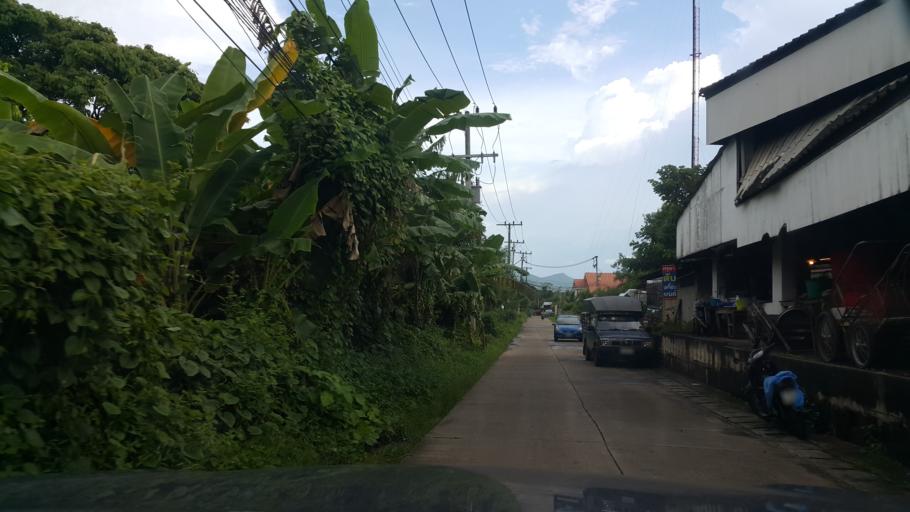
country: TH
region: Lampang
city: Thoen
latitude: 17.6105
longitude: 99.2160
